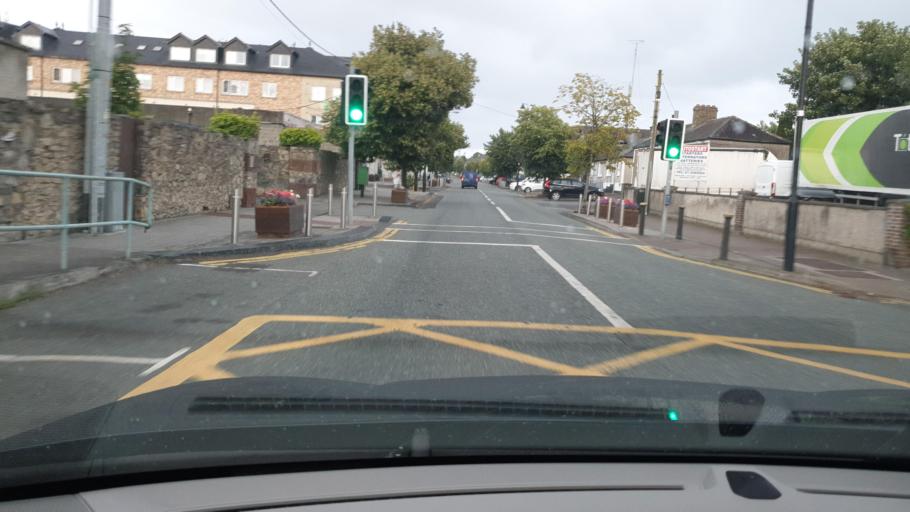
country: IE
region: Leinster
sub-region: South Dublin
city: Rathcoole
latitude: 53.2812
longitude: -6.4724
